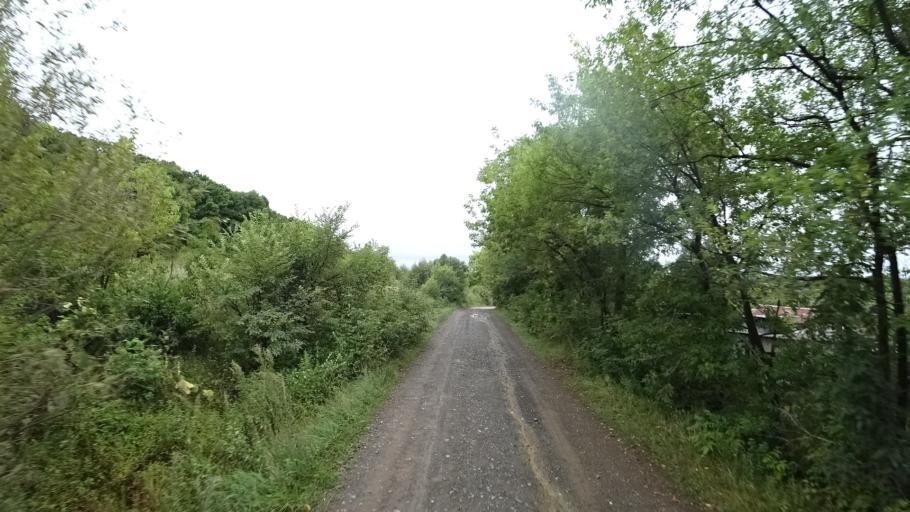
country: RU
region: Primorskiy
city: Monastyrishche
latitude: 44.2753
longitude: 132.4082
